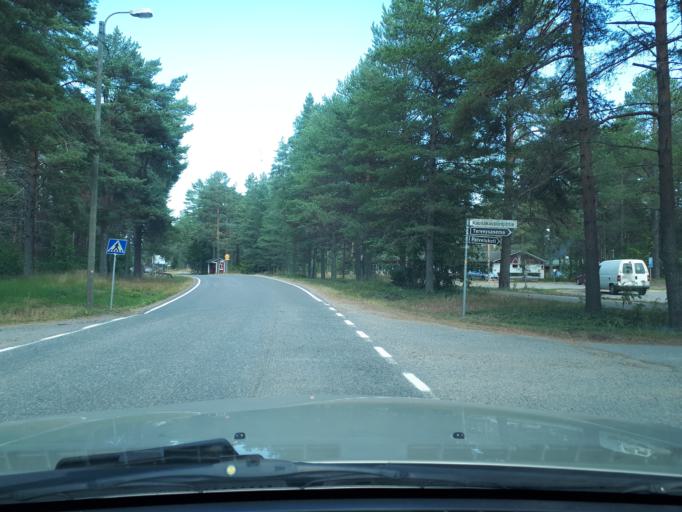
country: FI
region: Northern Ostrobothnia
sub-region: Oulu
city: Hailuoto
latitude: 65.0167
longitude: 24.7371
